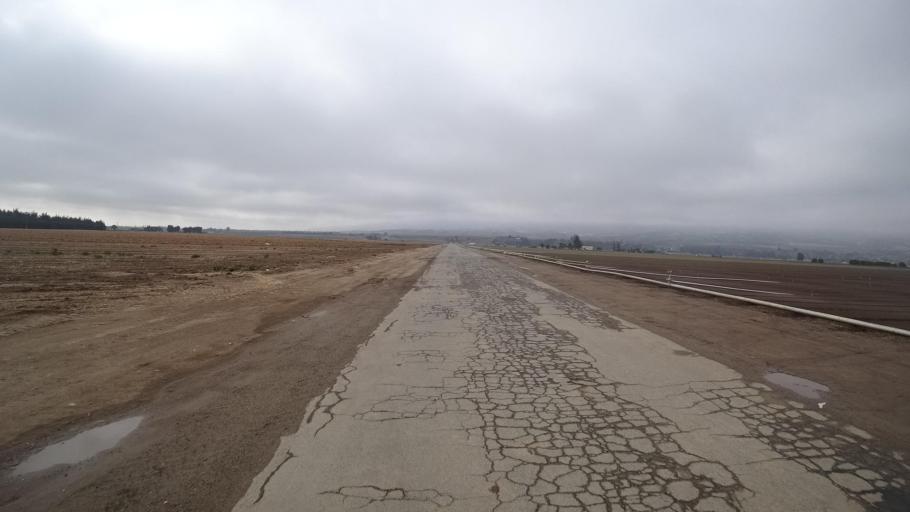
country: US
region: California
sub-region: Monterey County
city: Soledad
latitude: 36.3918
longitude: -121.3352
